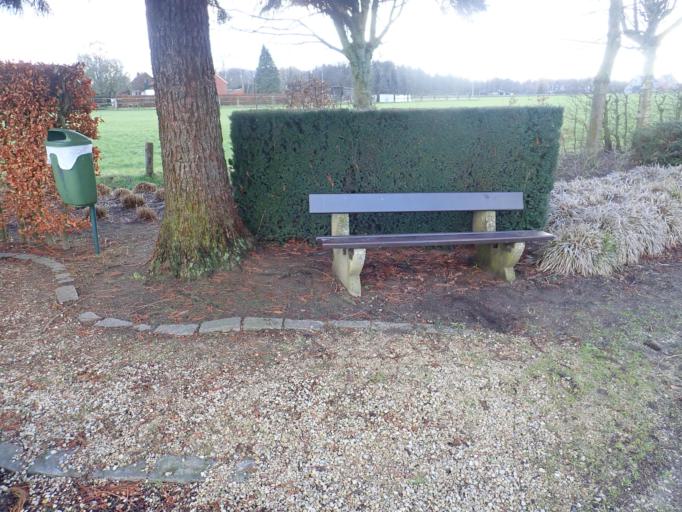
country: BE
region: Flanders
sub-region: Provincie Antwerpen
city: Zoersel
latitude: 51.2246
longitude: 4.7067
